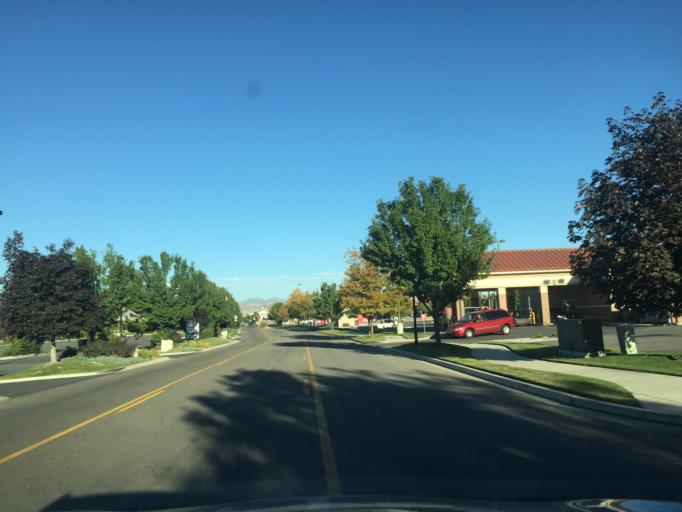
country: US
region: Utah
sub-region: Utah County
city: American Fork
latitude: 40.3852
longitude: -111.8195
